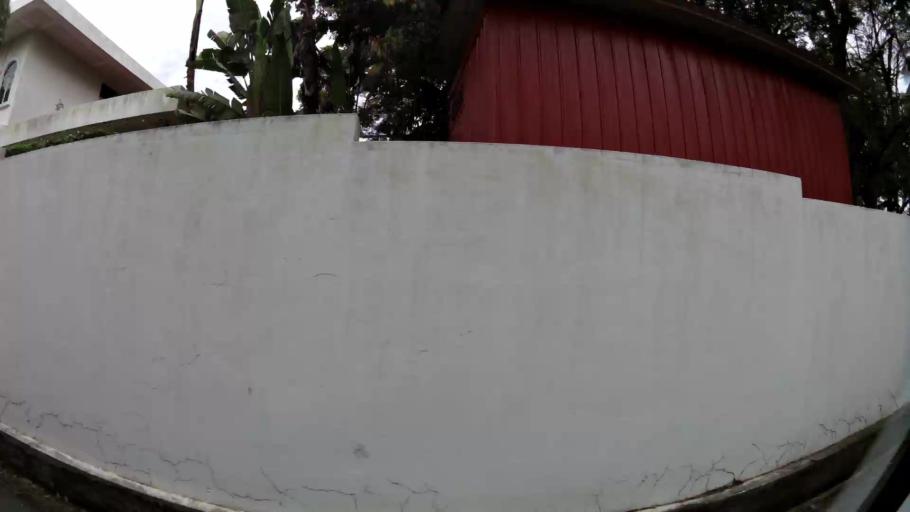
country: BN
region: Brunei and Muara
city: Bandar Seri Begawan
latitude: 4.8901
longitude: 114.9006
